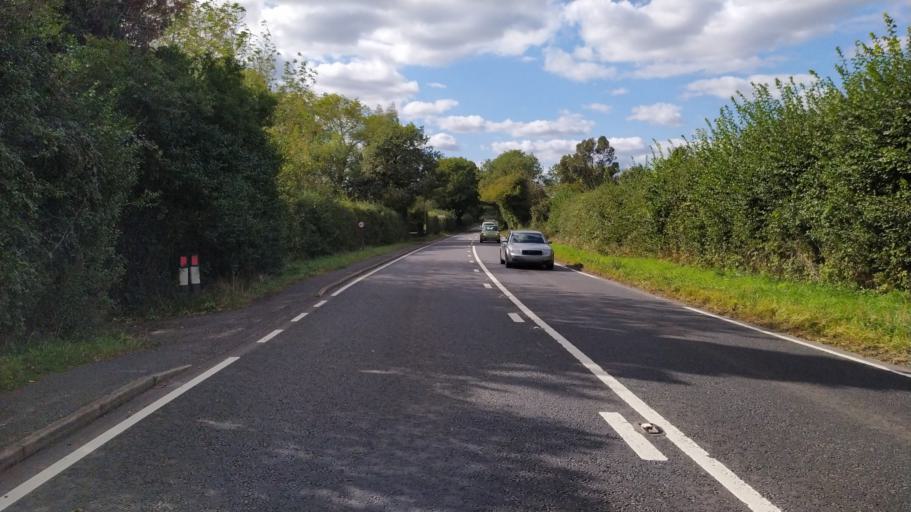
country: GB
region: England
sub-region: West Berkshire
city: Stratfield Mortimer
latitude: 51.3261
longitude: -1.0067
